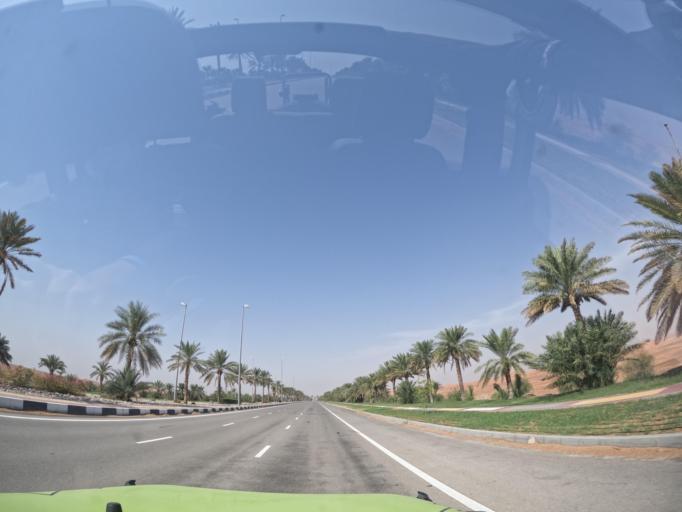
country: AE
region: Abu Dhabi
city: Al Ain
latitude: 24.2618
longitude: 55.6614
